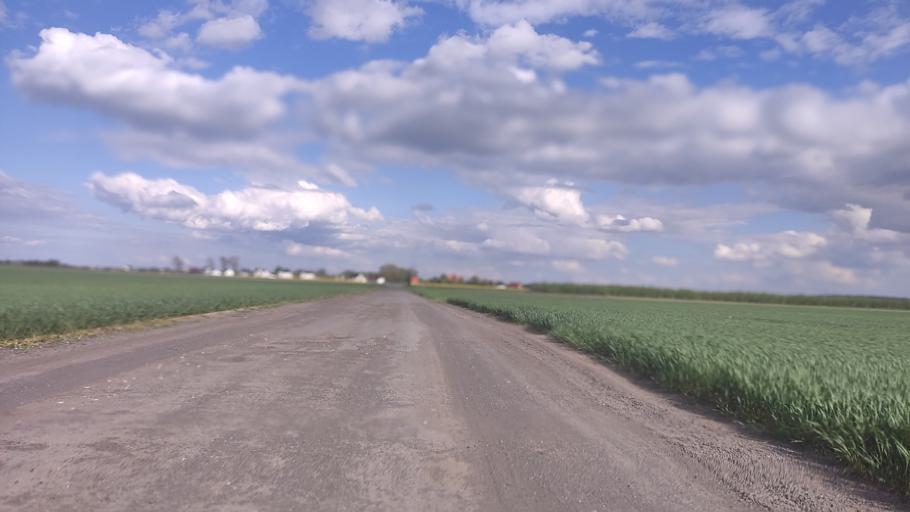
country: PL
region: Greater Poland Voivodeship
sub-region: Powiat poznanski
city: Swarzedz
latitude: 52.3871
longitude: 17.1345
